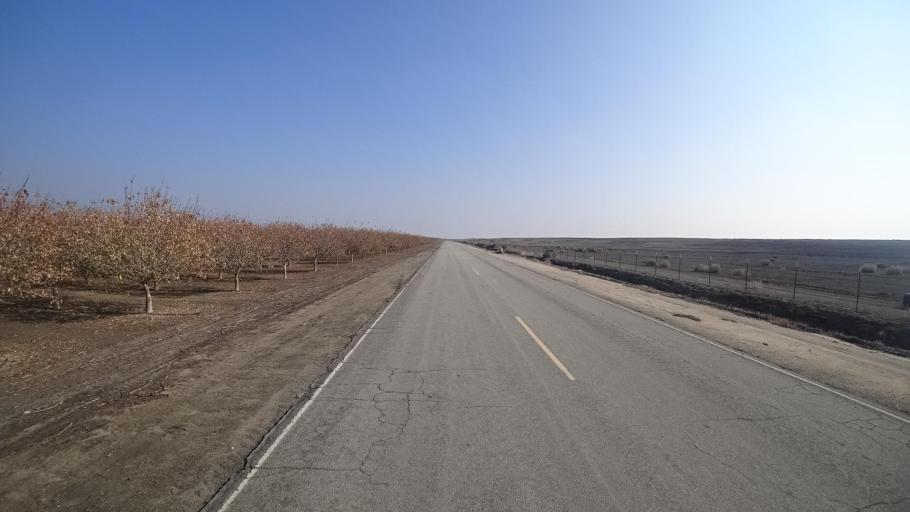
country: US
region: California
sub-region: Kern County
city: Buttonwillow
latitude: 35.3403
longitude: -119.3885
